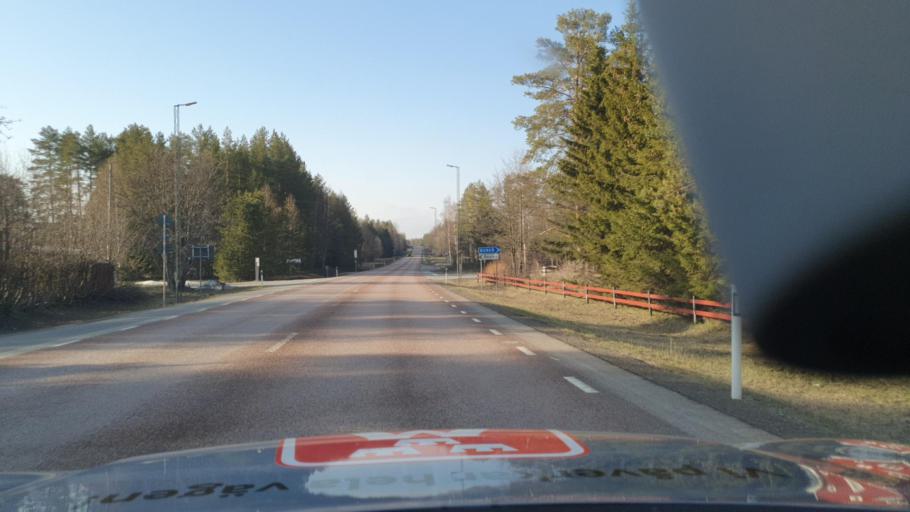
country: SE
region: Vaesterbotten
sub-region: Skelleftea Kommun
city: Burea
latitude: 64.6185
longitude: 21.1786
